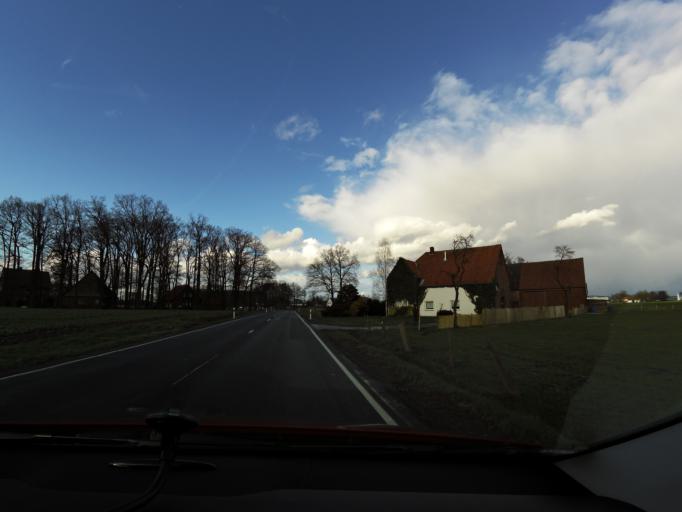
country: DE
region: North Rhine-Westphalia
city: Rietberg
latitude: 51.8682
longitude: 8.4515
